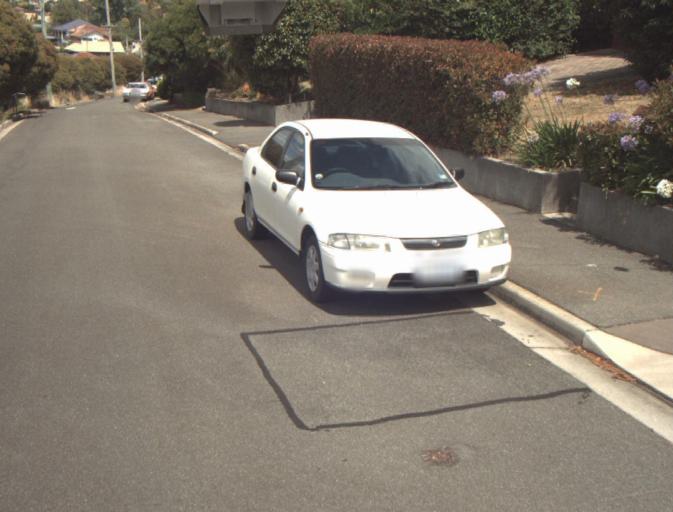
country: AU
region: Tasmania
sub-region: Launceston
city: Launceston
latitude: -41.4321
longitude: 147.1151
